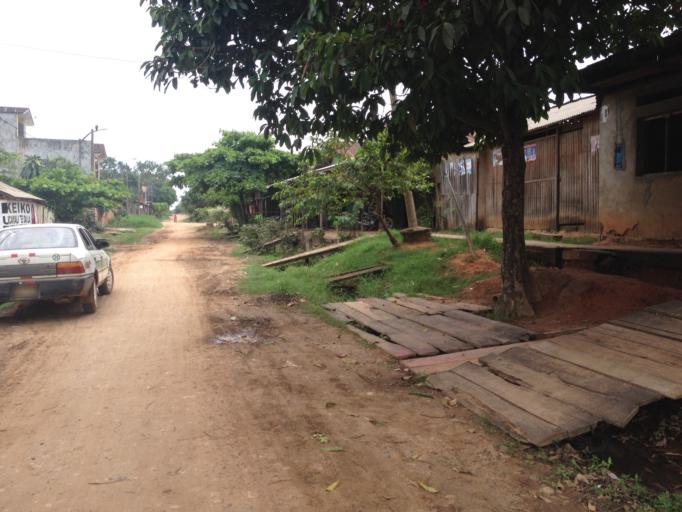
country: PE
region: Ucayali
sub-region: Provincia de Coronel Portillo
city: Pucallpa
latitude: -8.3837
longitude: -74.5575
